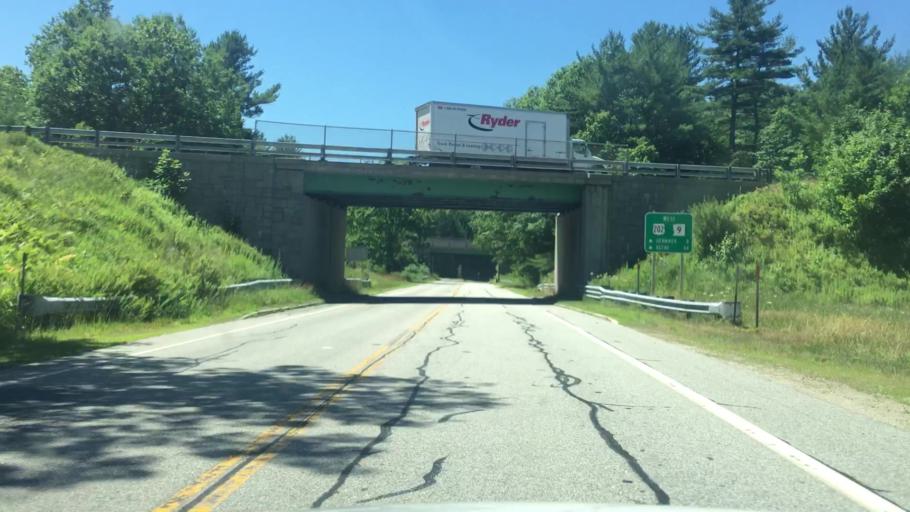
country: US
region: New Hampshire
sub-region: Merrimack County
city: Hopkinton
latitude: 43.1823
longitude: -71.6881
